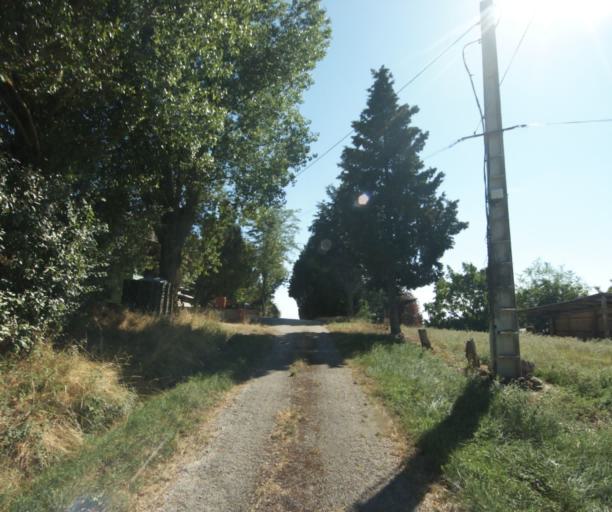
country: FR
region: Midi-Pyrenees
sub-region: Departement de la Haute-Garonne
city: Saint-Felix-Lauragais
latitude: 43.5183
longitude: 1.9075
